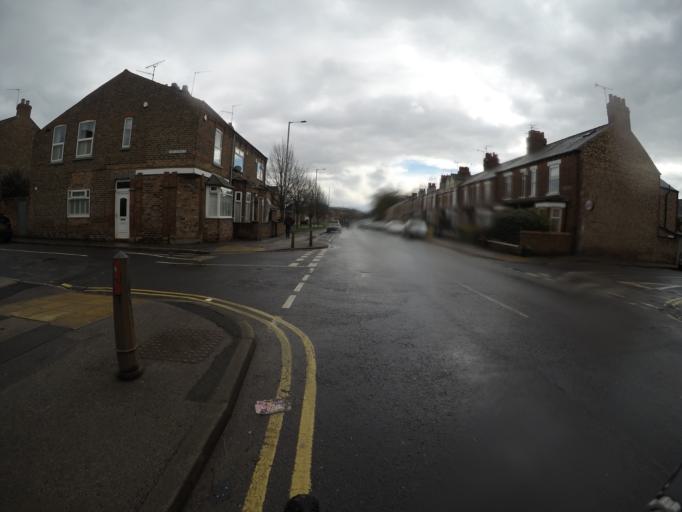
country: GB
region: England
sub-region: City of York
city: York
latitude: 53.9607
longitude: -1.1132
